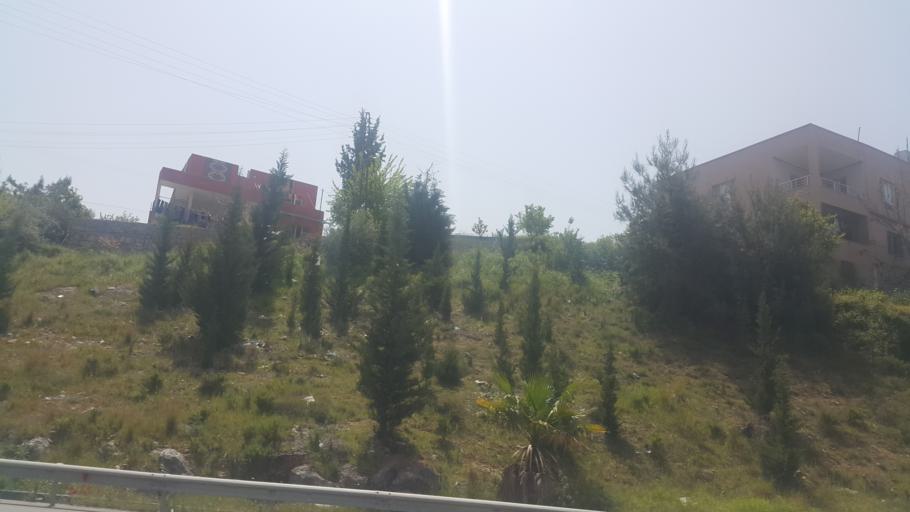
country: TR
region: Hatay
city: Iskenderun
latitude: 36.5646
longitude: 36.1778
